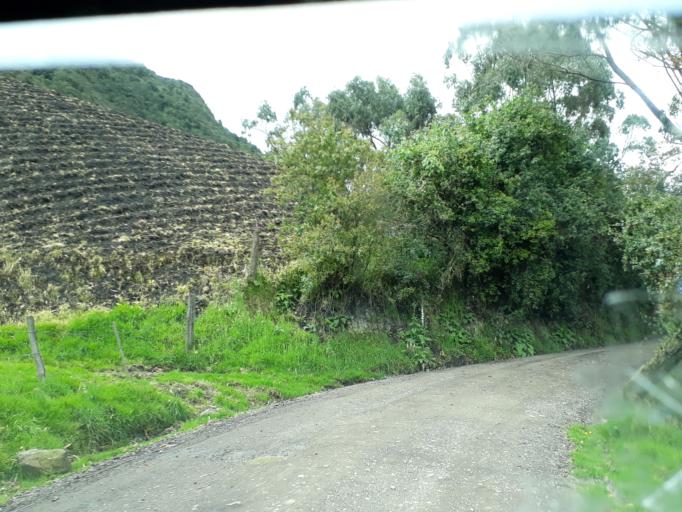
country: CO
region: Cundinamarca
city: Cogua
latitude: 5.1651
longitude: -73.9964
